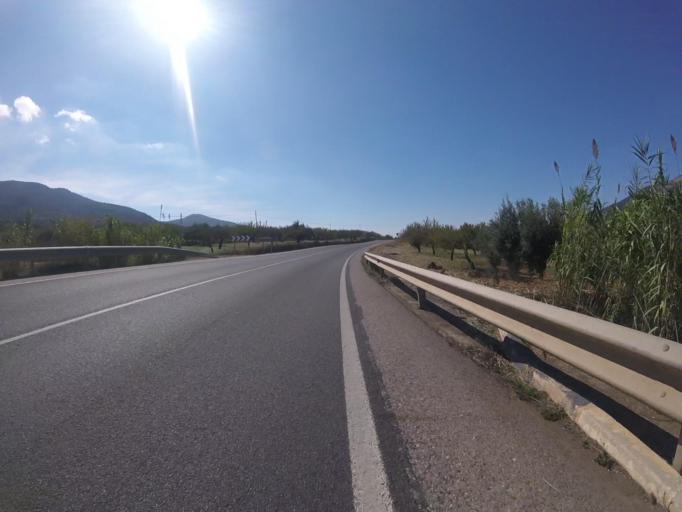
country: ES
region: Valencia
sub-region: Provincia de Castello
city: Sierra-Engarceran
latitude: 40.3051
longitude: -0.0417
